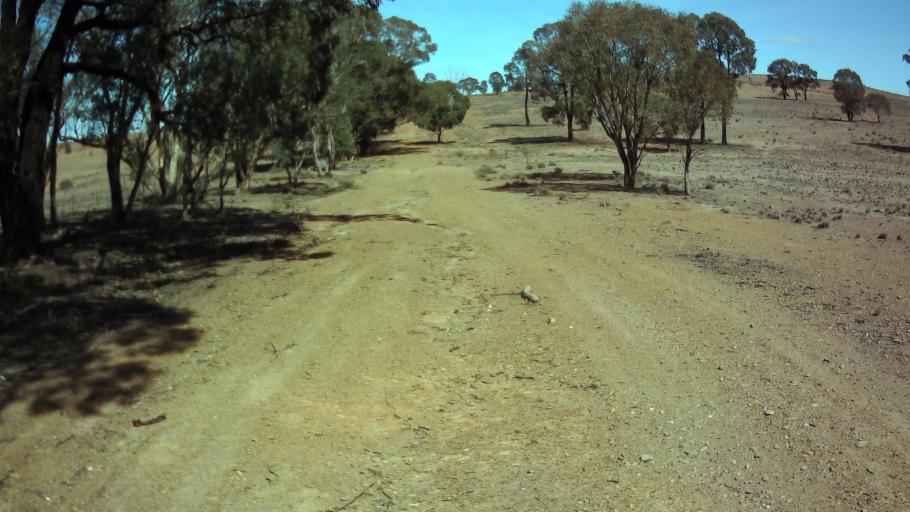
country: AU
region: New South Wales
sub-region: Weddin
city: Grenfell
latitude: -33.7198
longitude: 147.8333
